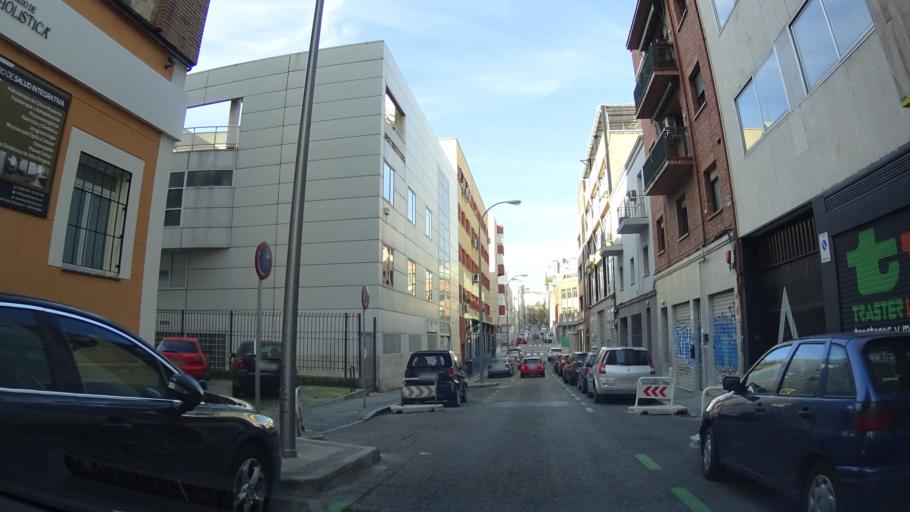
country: ES
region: Madrid
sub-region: Provincia de Madrid
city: Chamartin
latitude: 40.4472
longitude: -3.6701
